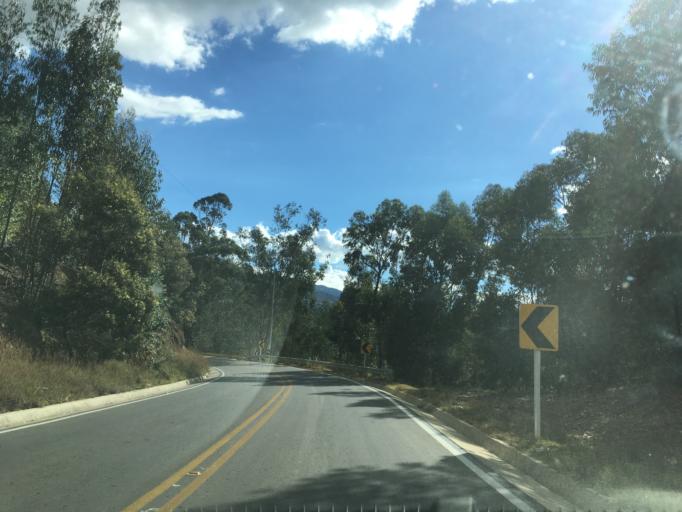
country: CO
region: Boyaca
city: Firavitoba
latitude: 5.6115
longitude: -73.0204
